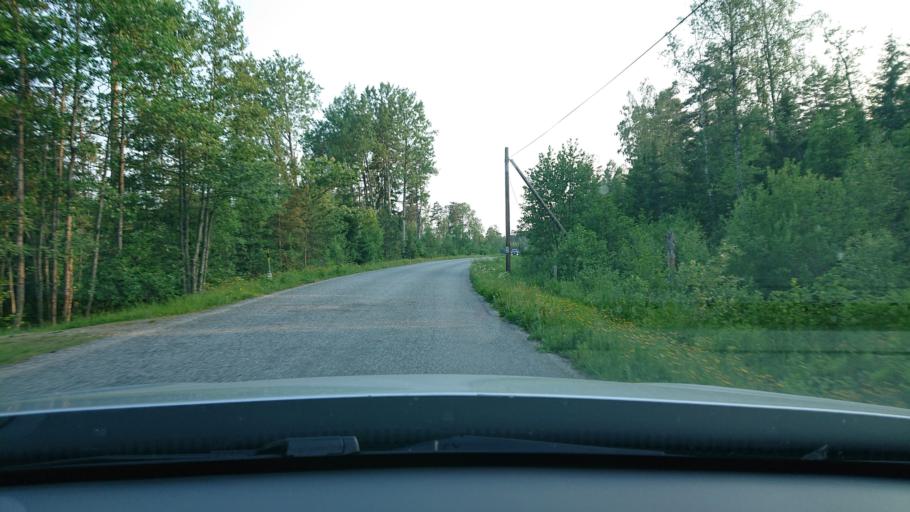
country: SE
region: Stockholm
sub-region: Osterakers Kommun
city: Akersberga
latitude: 59.5172
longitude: 18.3269
